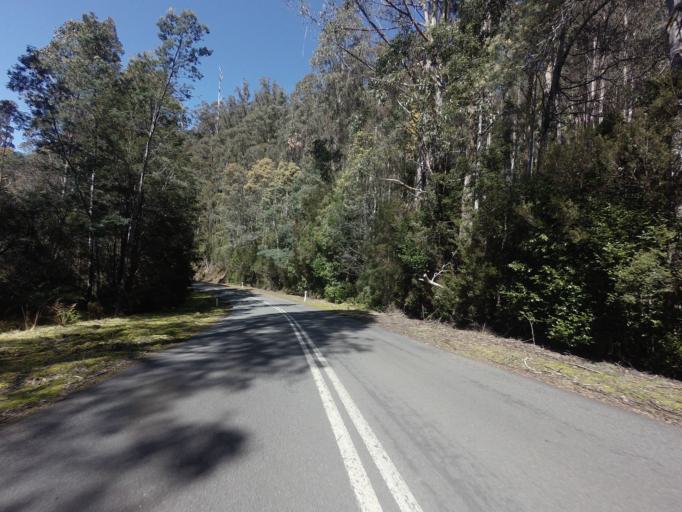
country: AU
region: Tasmania
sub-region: Derwent Valley
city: New Norfolk
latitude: -42.7490
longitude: 146.5034
